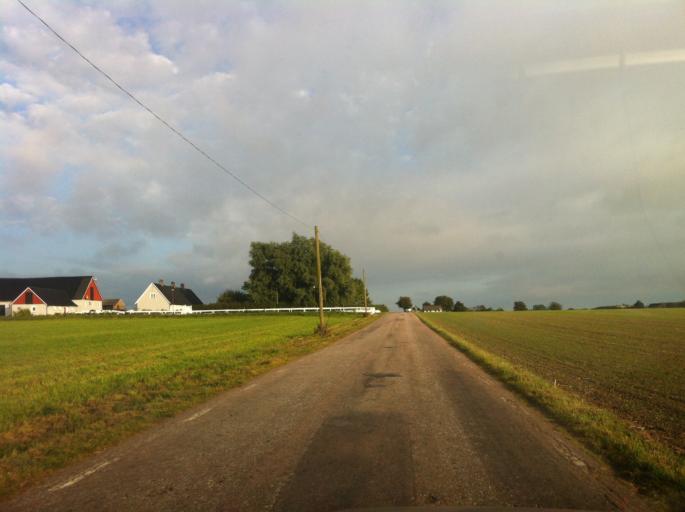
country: SE
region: Skane
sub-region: Helsingborg
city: Barslov
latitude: 55.9767
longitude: 12.8617
